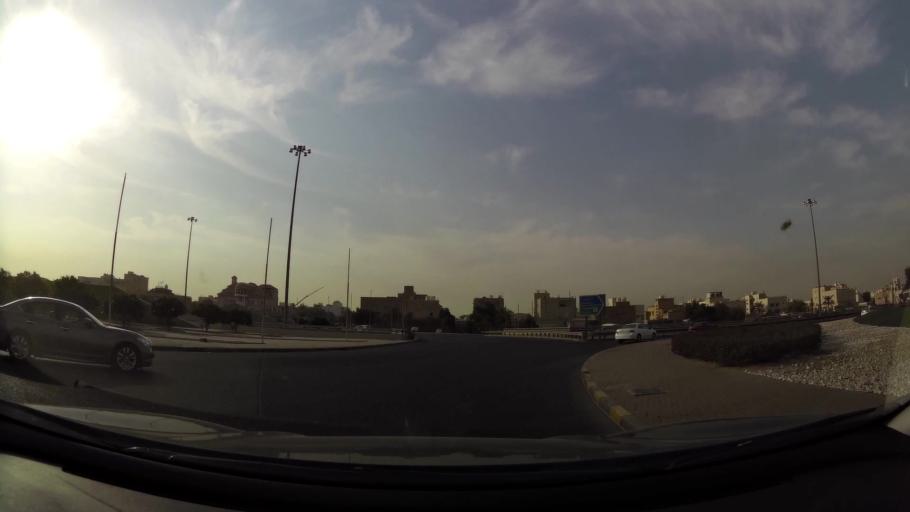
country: KW
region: Muhafazat Hawalli
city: As Salimiyah
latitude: 29.3264
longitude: 48.0770
